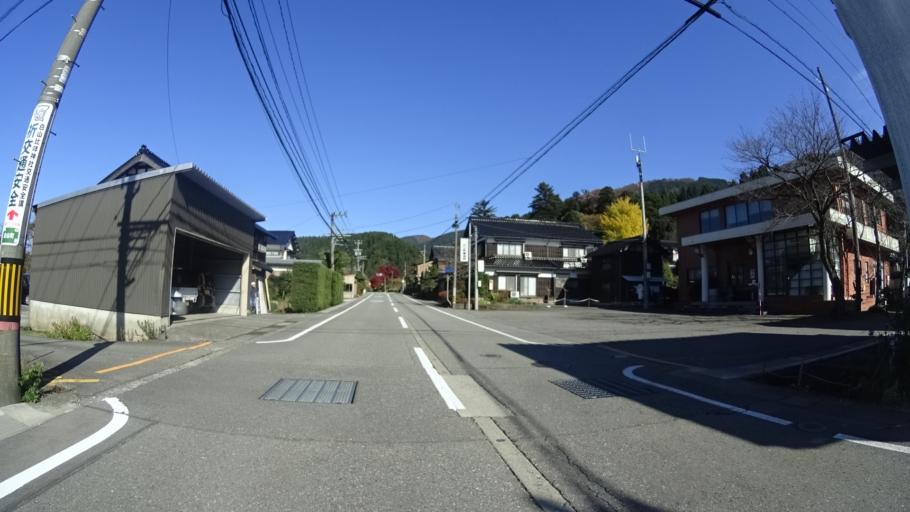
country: JP
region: Ishikawa
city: Tsurugi-asahimachi
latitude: 36.4326
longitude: 136.6341
